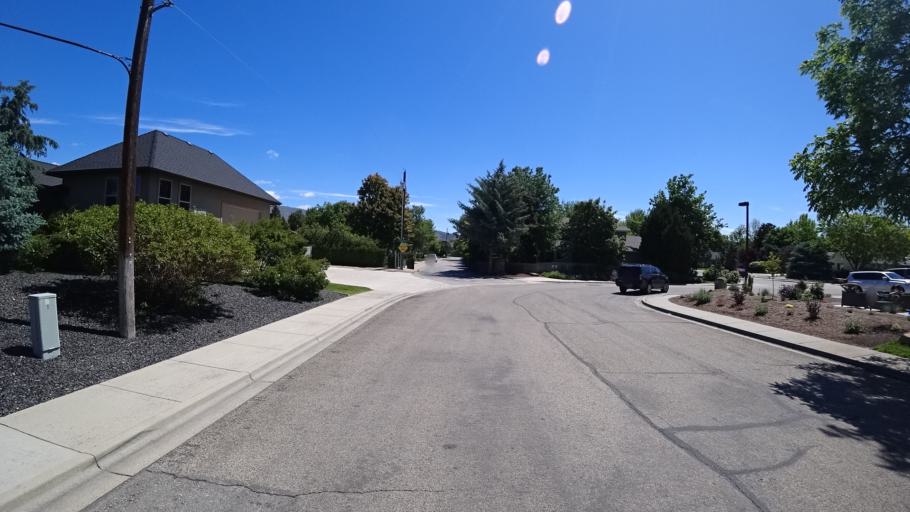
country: US
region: Idaho
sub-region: Ada County
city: Boise
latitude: 43.5678
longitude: -116.1530
